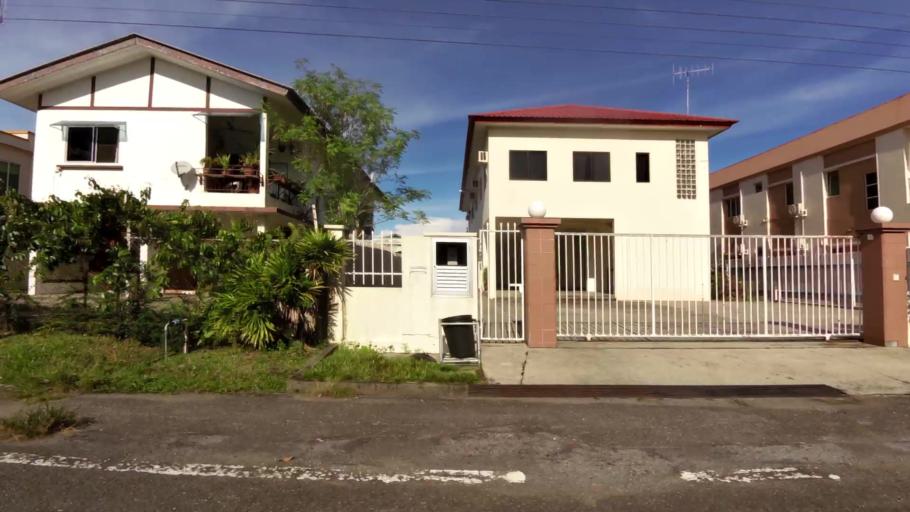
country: BN
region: Belait
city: Kuala Belait
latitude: 4.5843
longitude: 114.1937
